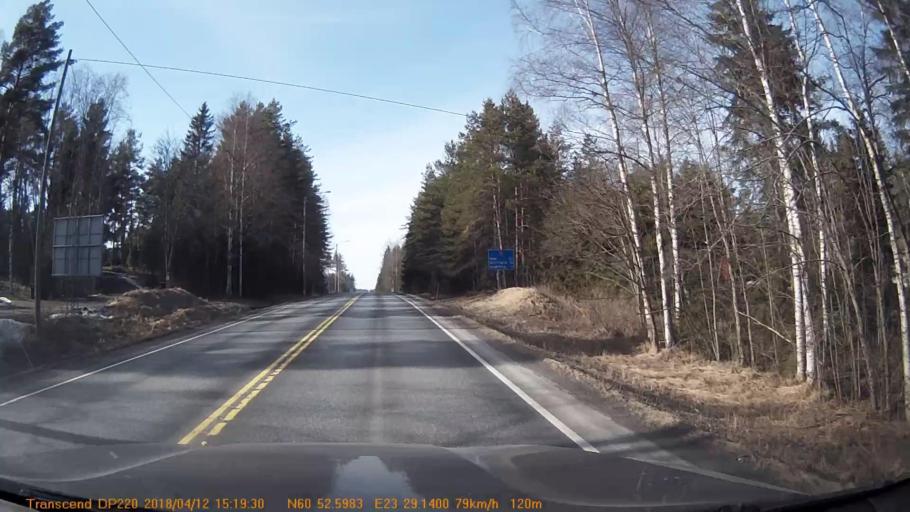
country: FI
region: Haeme
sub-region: Forssa
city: Jokioinen
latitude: 60.8770
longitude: 23.4851
